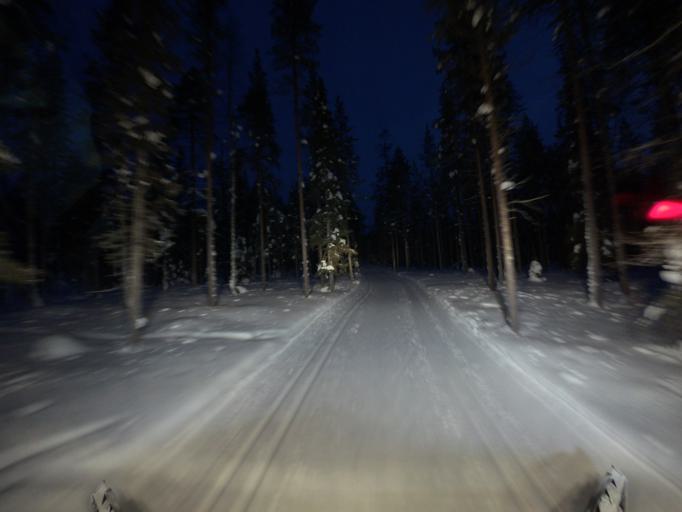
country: FI
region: Lapland
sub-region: Tunturi-Lappi
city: Kolari
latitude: 67.5955
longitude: 24.1095
